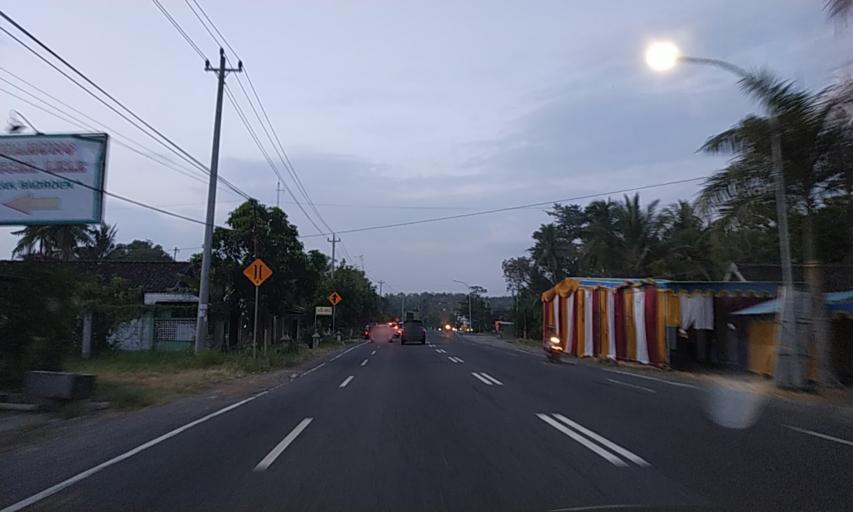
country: ID
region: Daerah Istimewa Yogyakarta
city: Srandakan
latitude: -7.8609
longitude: 110.2118
